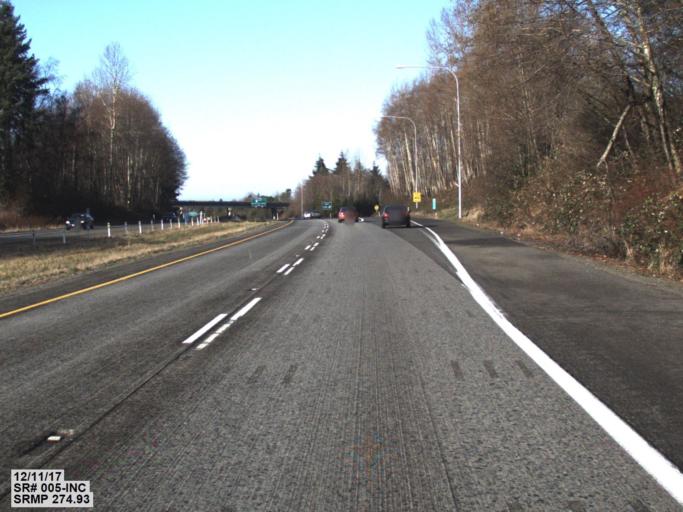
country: US
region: Washington
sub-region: Whatcom County
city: Blaine
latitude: 48.9844
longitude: -122.7330
